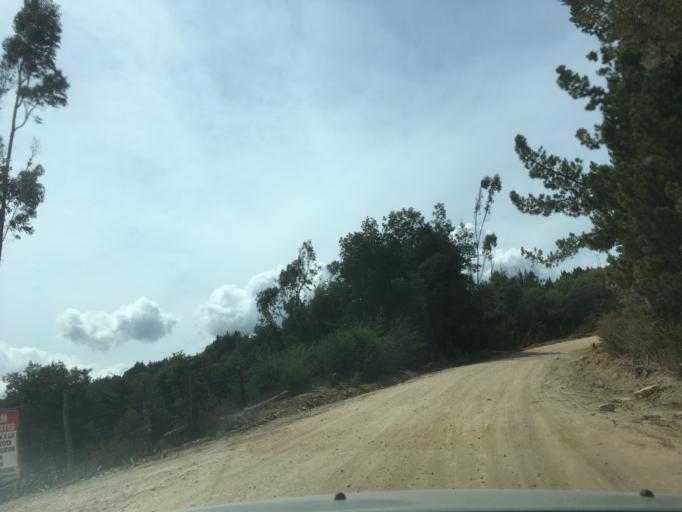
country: CO
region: Boyaca
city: Aquitania
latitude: 5.5692
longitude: -72.9453
